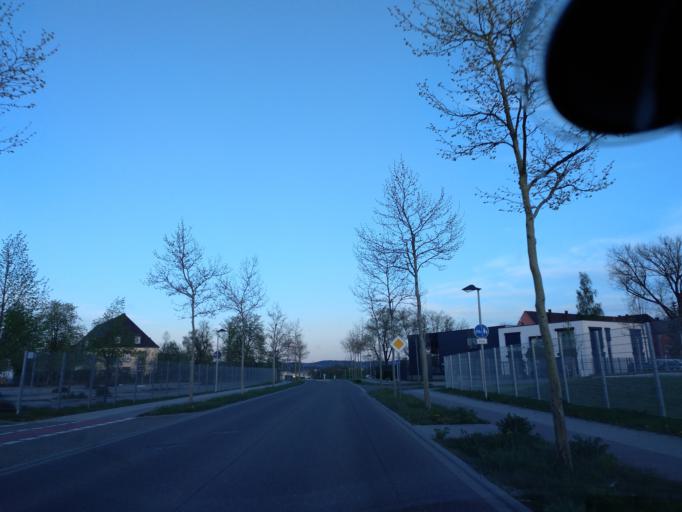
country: DE
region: Baden-Wuerttemberg
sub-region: Regierungsbezirk Stuttgart
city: Crailsheim
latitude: 49.1354
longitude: 10.0527
